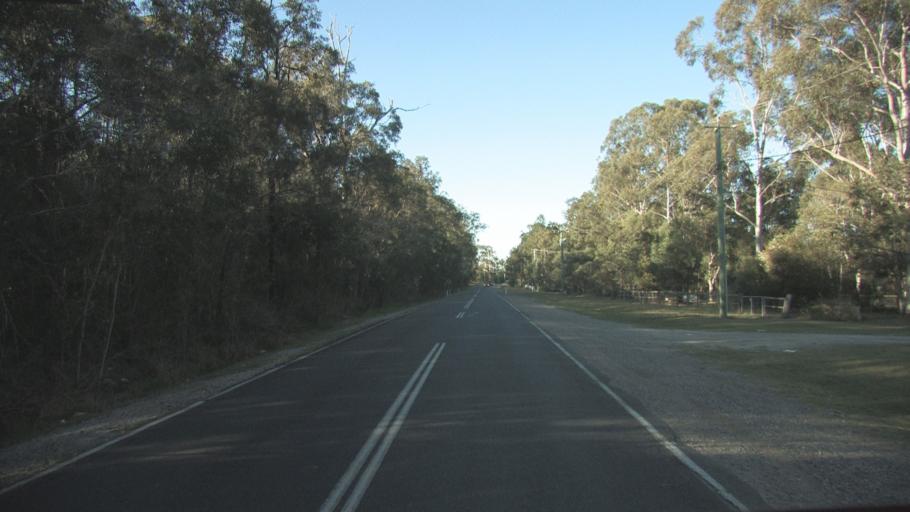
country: AU
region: Queensland
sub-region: Logan
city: Chambers Flat
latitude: -27.7774
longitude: 153.0748
